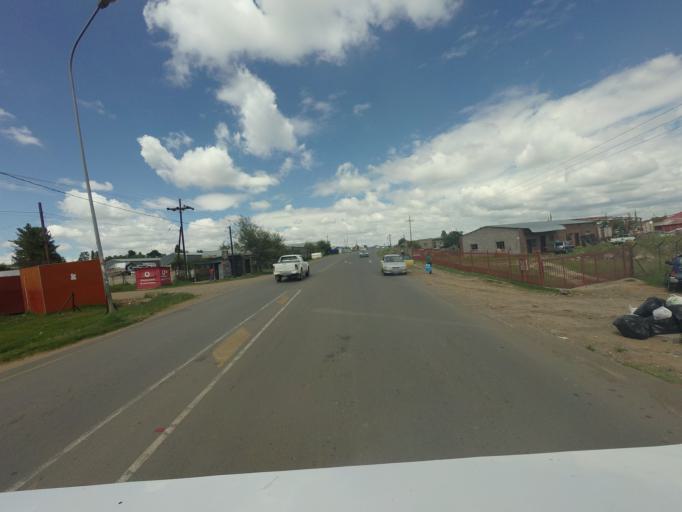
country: LS
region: Maseru
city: Maseru
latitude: -29.2843
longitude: 27.5270
